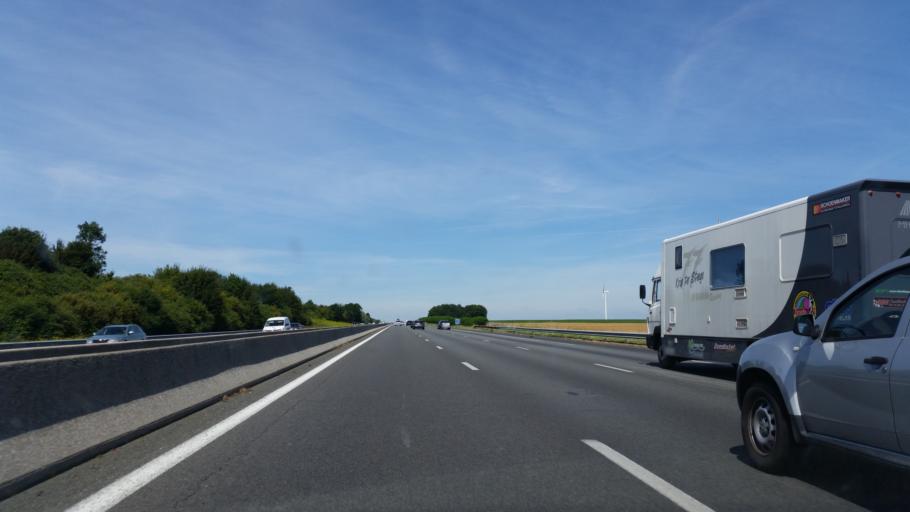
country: FR
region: Nord-Pas-de-Calais
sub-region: Departement du Pas-de-Calais
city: Croisilles
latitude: 50.2078
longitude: 2.8650
